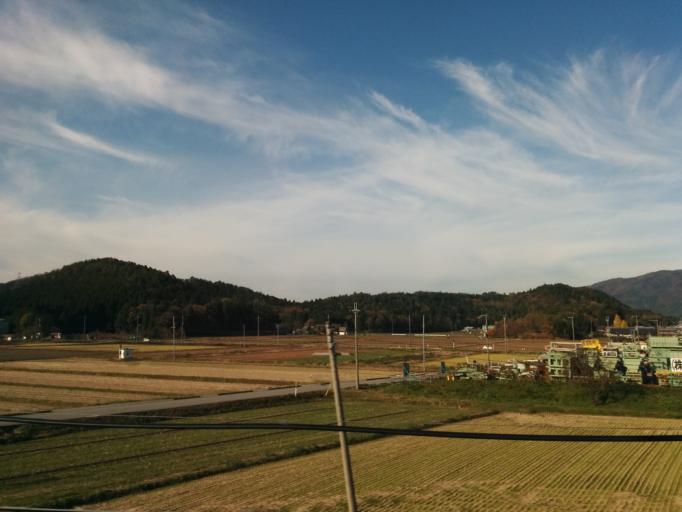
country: JP
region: Shiga Prefecture
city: Nagahama
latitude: 35.3656
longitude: 136.3555
